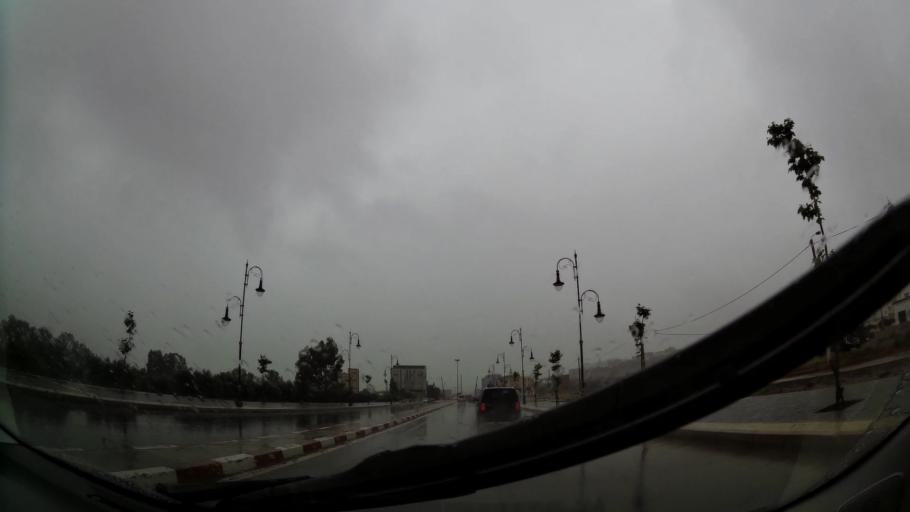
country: MA
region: Taza-Al Hoceima-Taounate
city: Imzourene
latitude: 35.1375
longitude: -3.8474
